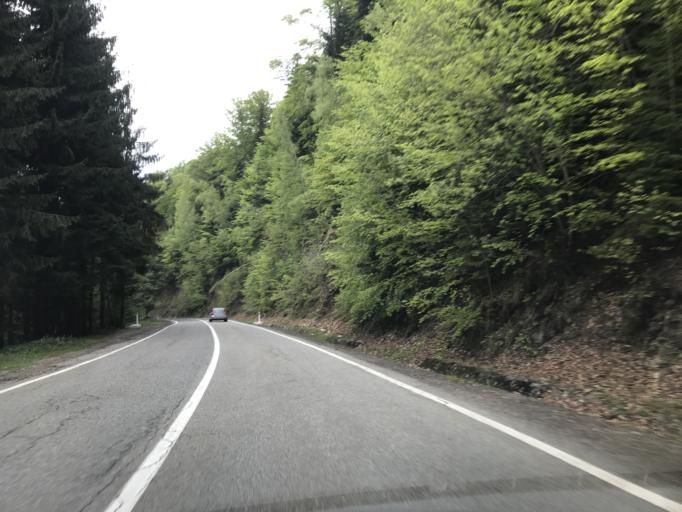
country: RO
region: Sibiu
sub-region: Comuna Cartisoara
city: Cartisoara
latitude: 45.6662
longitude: 24.5939
